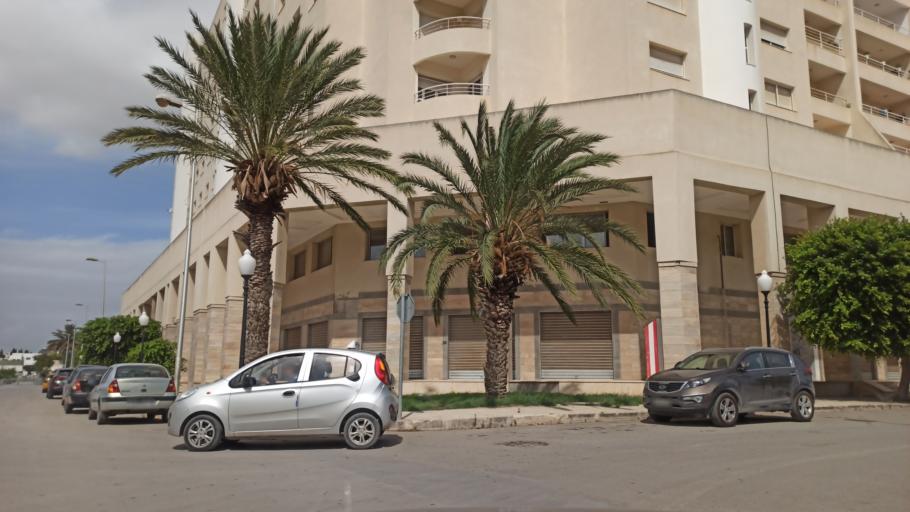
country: TN
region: Ariana
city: Ariana
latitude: 36.8483
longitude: 10.1901
